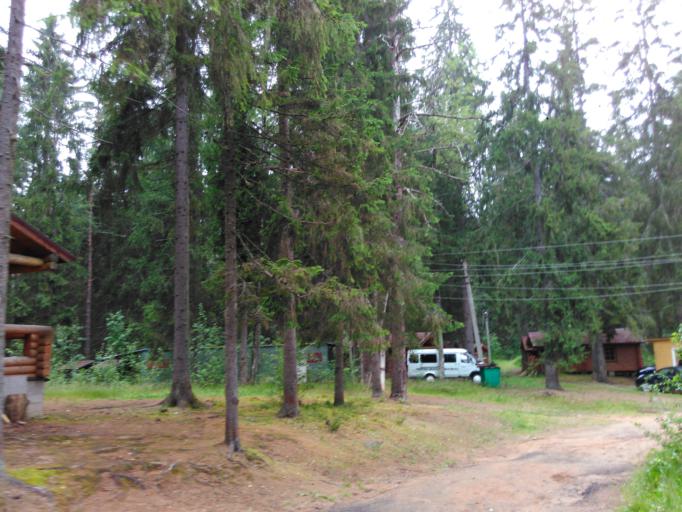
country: RU
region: Tverskaya
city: Ostashkov
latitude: 57.2060
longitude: 32.9801
